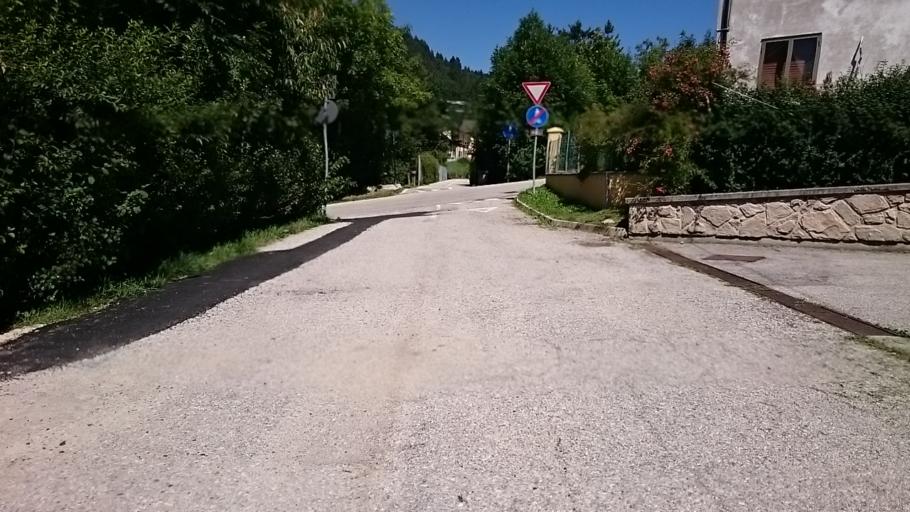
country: IT
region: Veneto
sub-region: Provincia di Belluno
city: Pieve di Cadore
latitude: 46.4230
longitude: 12.3615
